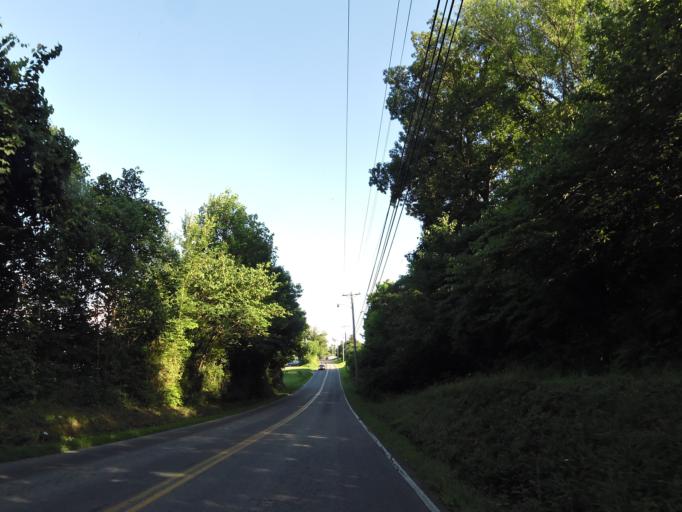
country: US
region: Tennessee
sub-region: Blount County
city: Maryville
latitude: 35.7394
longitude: -83.9548
